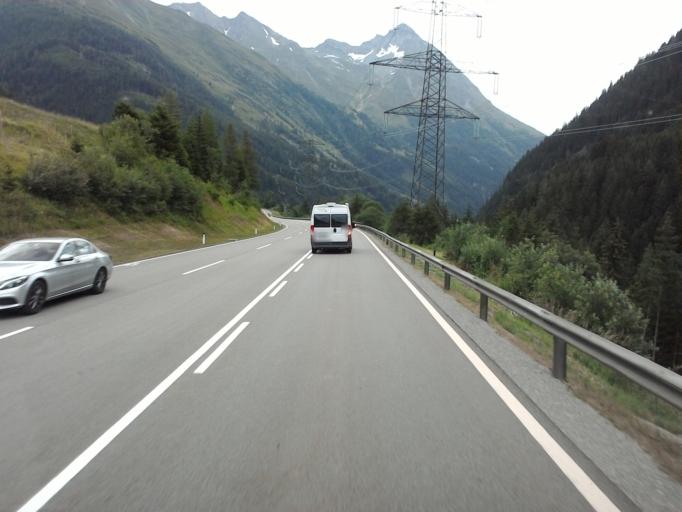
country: AT
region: Tyrol
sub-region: Politischer Bezirk Lienz
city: Matrei in Osttirol
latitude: 47.0938
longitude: 12.5199
